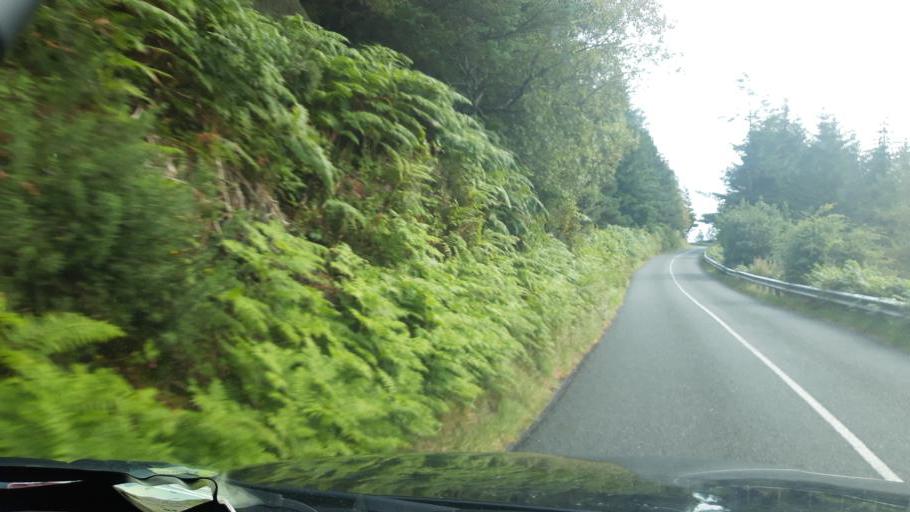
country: IE
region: Leinster
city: Ballinteer
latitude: 53.2301
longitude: -6.2695
